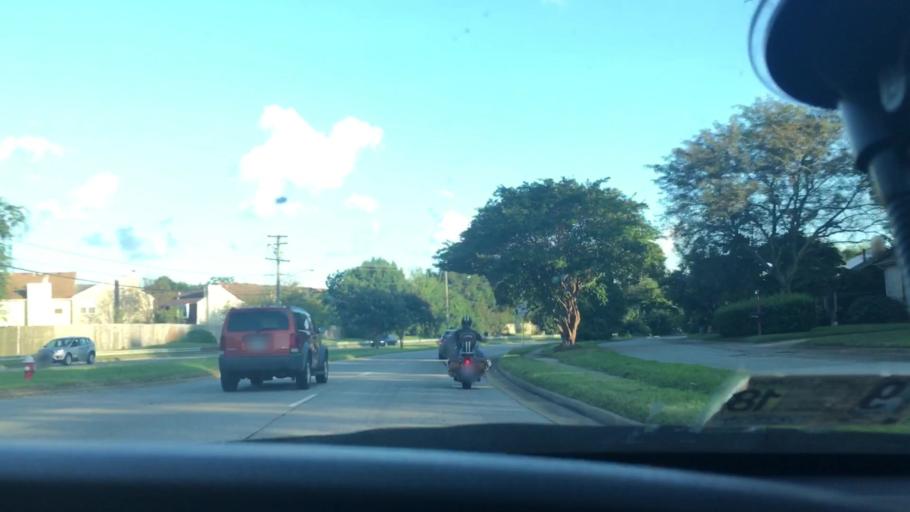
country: US
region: Virginia
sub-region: City of Chesapeake
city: Chesapeake
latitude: 36.8828
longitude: -76.1337
